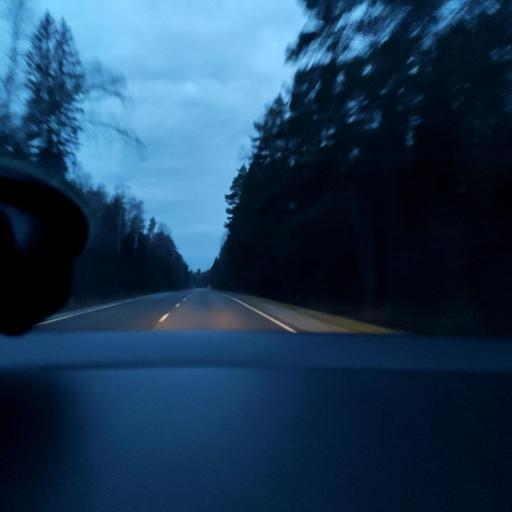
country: RU
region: Moskovskaya
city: Shaturtorf
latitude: 55.4303
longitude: 39.3690
